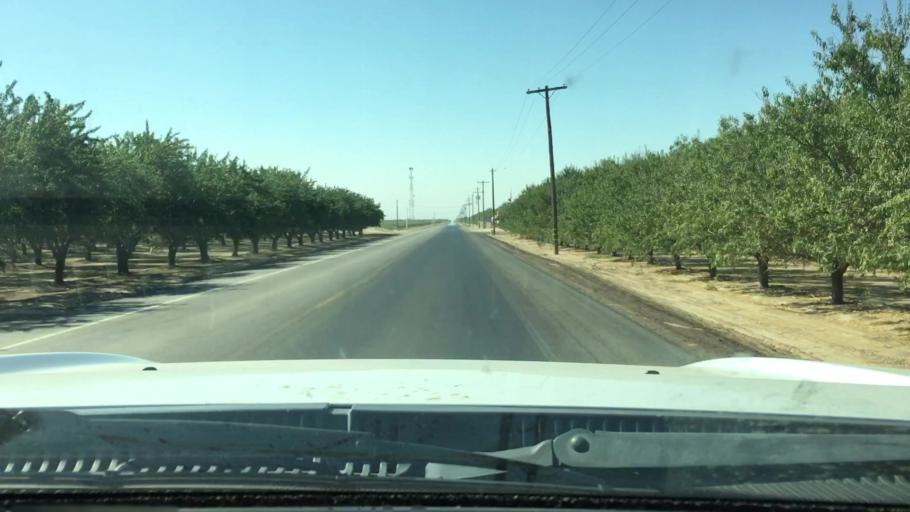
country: US
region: California
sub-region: Kern County
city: Wasco
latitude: 35.5951
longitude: -119.4736
